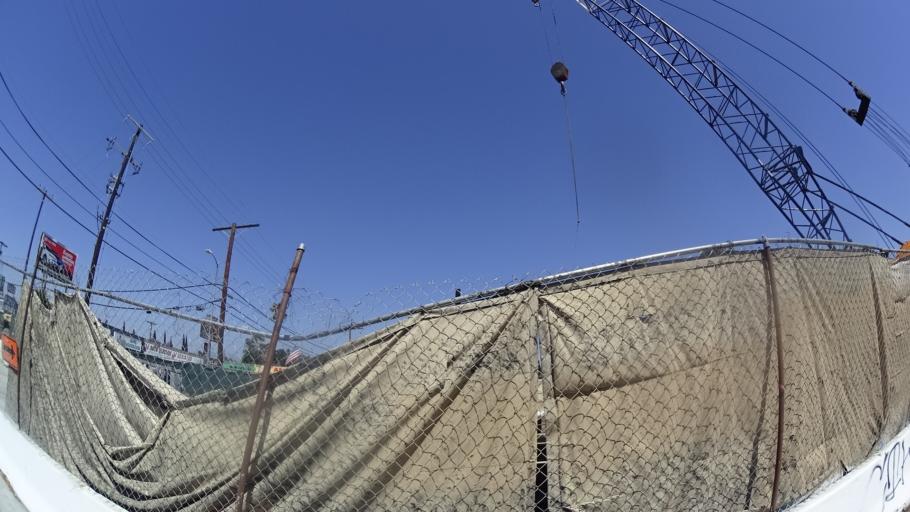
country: US
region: California
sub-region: Los Angeles County
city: North Hollywood
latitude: 34.1921
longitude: -118.3879
